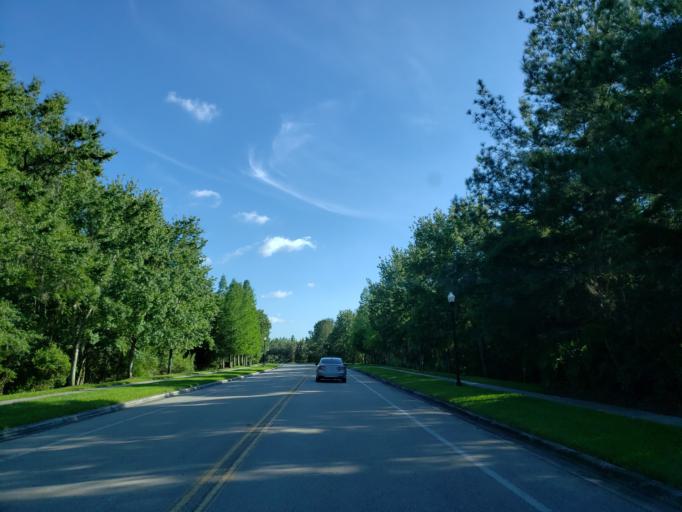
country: US
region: Florida
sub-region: Pasco County
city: Wesley Chapel
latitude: 28.2164
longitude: -82.3647
